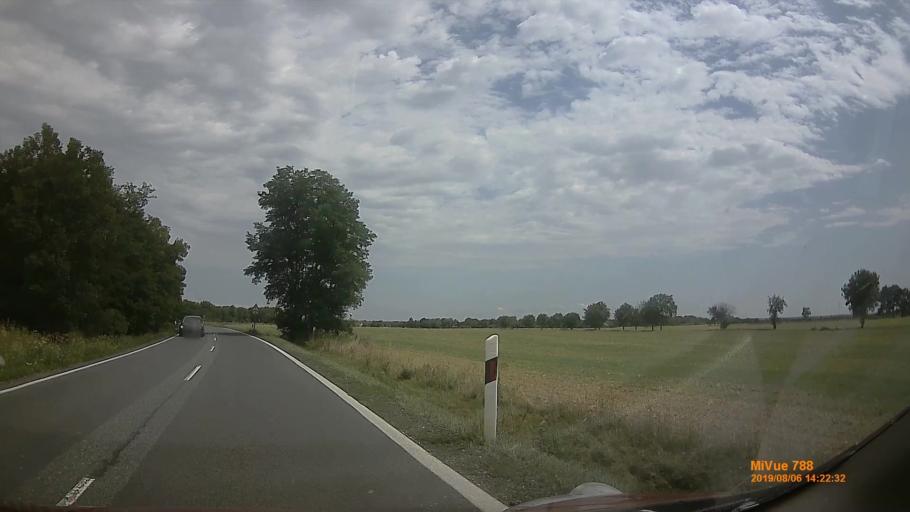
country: HU
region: Vas
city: Vep
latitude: 47.1601
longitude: 16.7926
